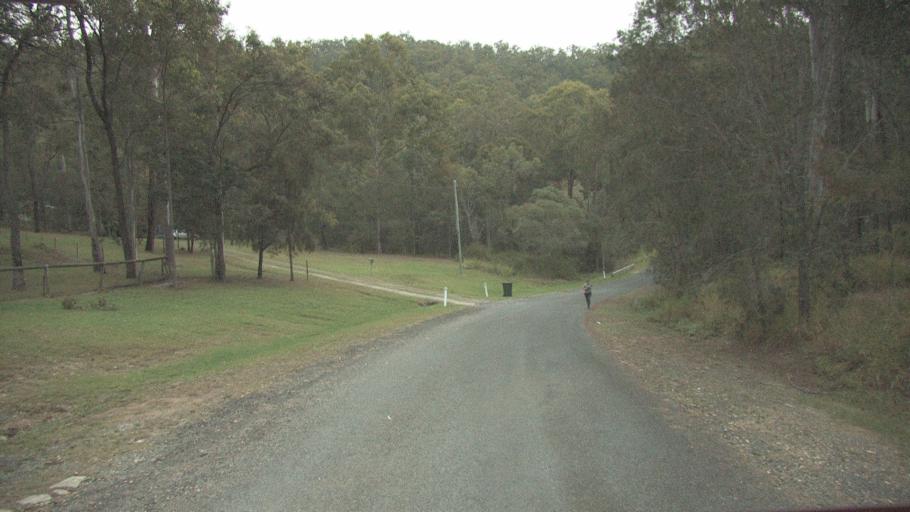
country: AU
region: Queensland
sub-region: Logan
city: Chambers Flat
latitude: -27.8250
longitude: 153.0913
